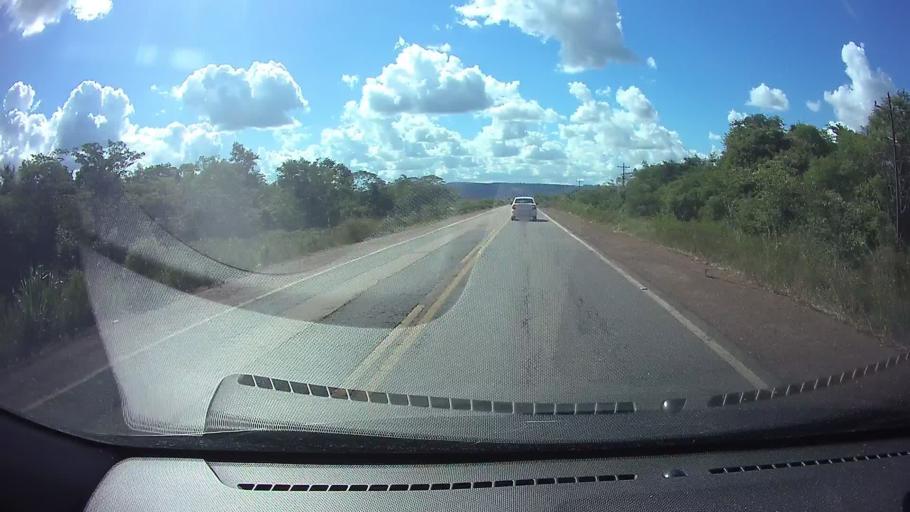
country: PY
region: Paraguari
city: Sapucai
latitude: -25.7163
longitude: -56.8354
